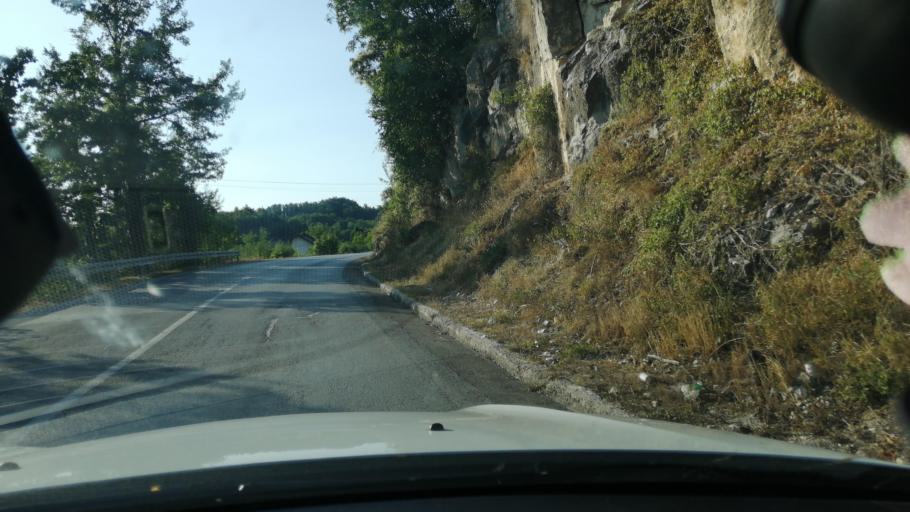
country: RS
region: Central Serbia
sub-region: Moravicki Okrug
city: Ivanjica
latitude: 43.6355
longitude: 20.2429
